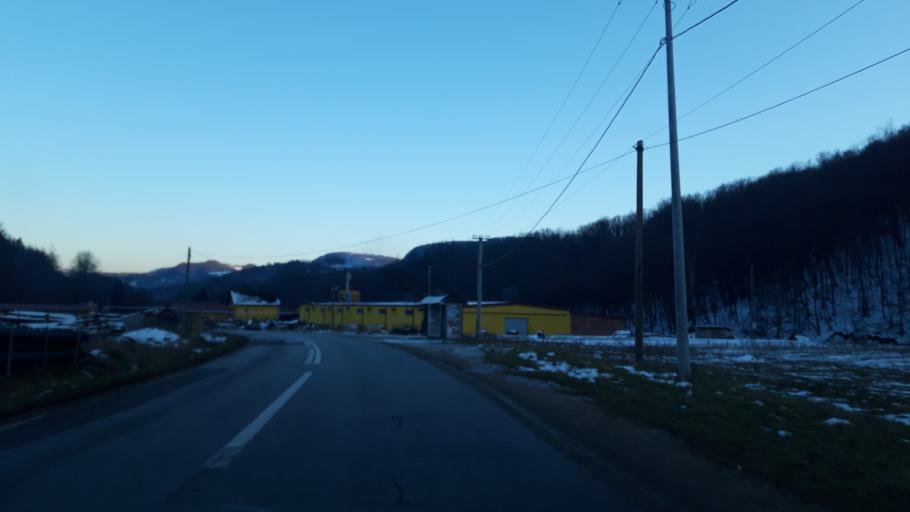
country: BA
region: Republika Srpska
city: Milici
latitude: 44.1666
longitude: 19.0351
